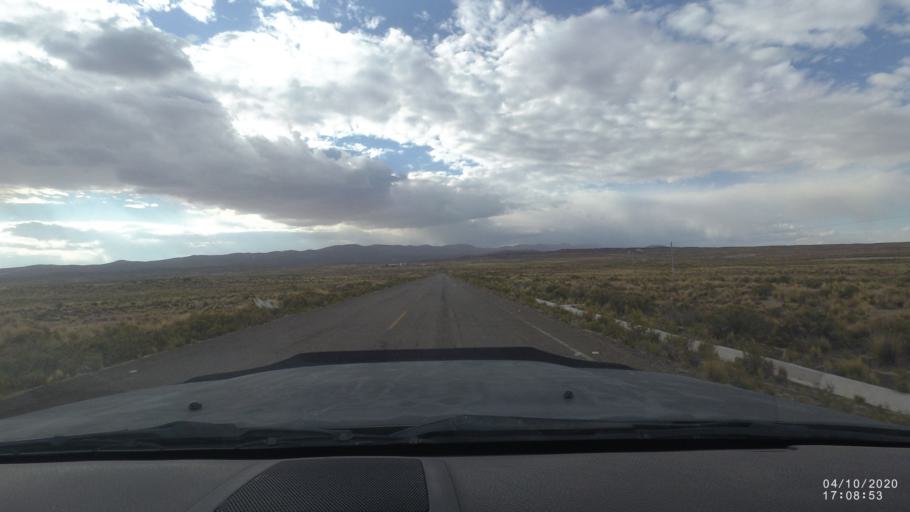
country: BO
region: Oruro
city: Oruro
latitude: -18.3445
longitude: -67.5771
